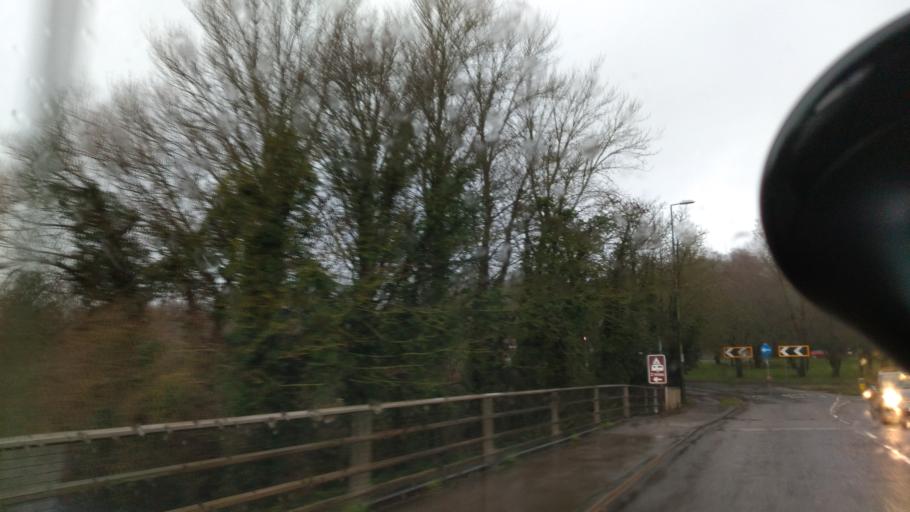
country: GB
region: England
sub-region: West Sussex
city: Arundel
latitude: 50.8521
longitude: -0.5604
